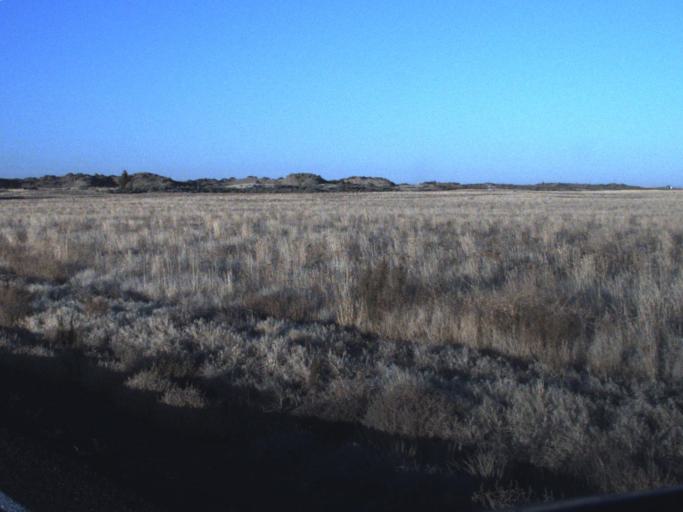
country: US
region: Washington
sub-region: Franklin County
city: Connell
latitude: 46.7677
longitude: -118.5475
